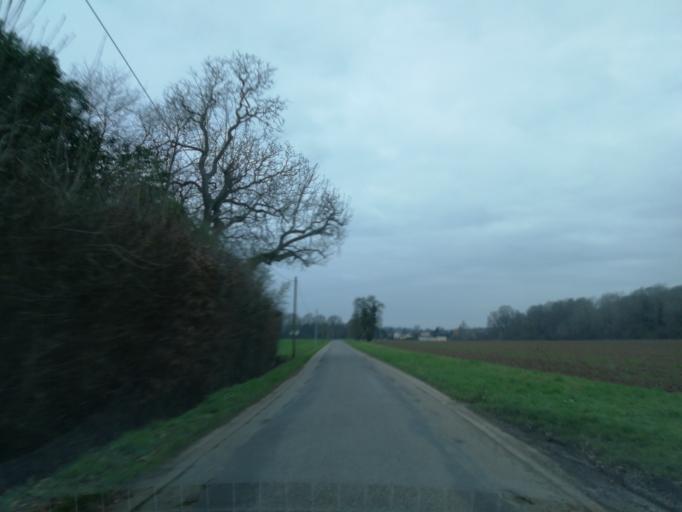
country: FR
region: Ile-de-France
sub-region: Departement de l'Essonne
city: Les Molieres
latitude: 48.6674
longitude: 2.0772
